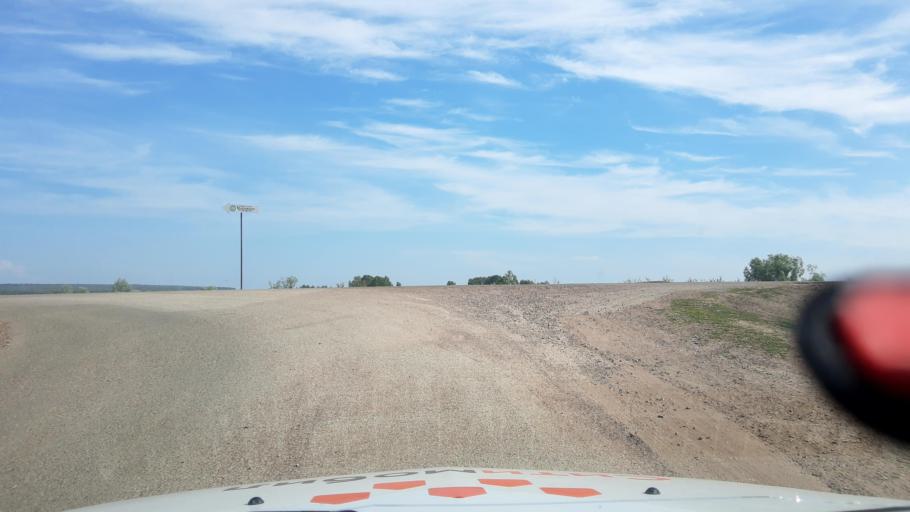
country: RU
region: Bashkortostan
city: Mikhaylovka
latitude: 54.9647
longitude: 55.8011
